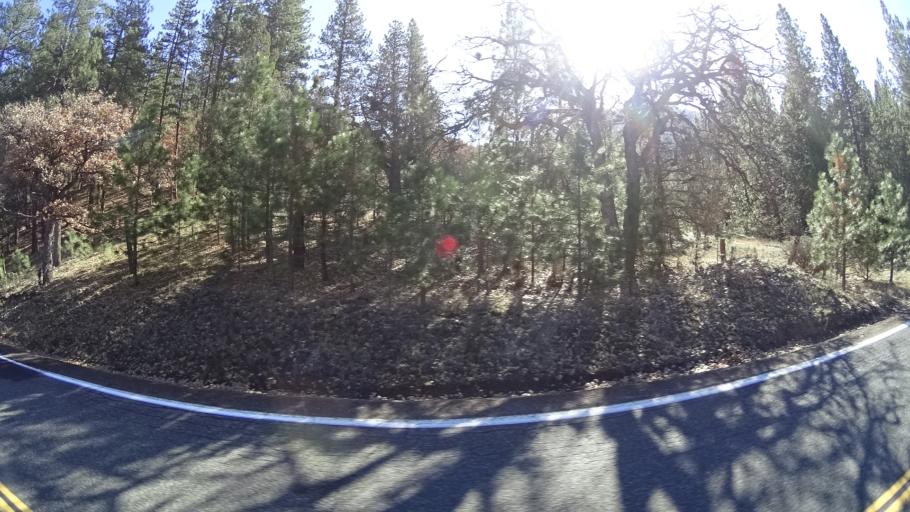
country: US
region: California
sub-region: Siskiyou County
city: Weed
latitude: 41.4674
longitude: -122.5962
